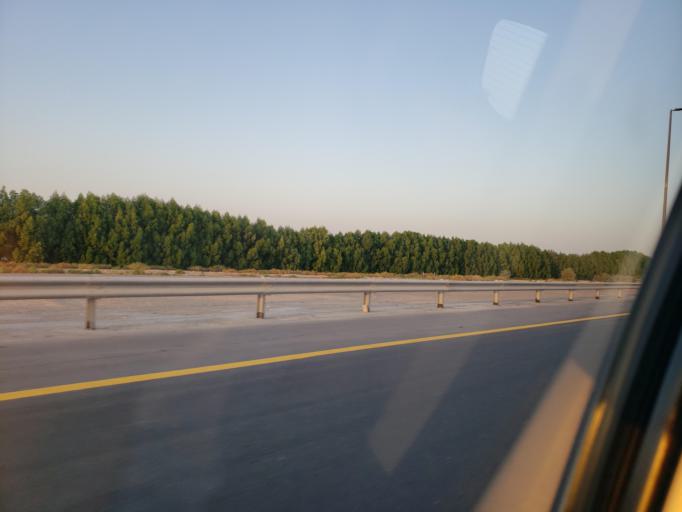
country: AE
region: Dubai
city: Dubai
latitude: 24.9552
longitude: 55.2246
